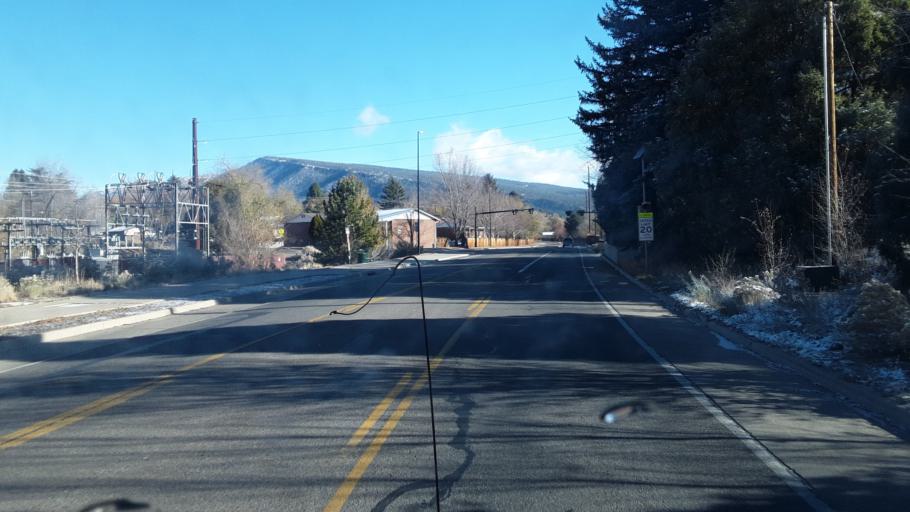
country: US
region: Colorado
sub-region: La Plata County
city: Durango
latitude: 37.2917
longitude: -107.8619
